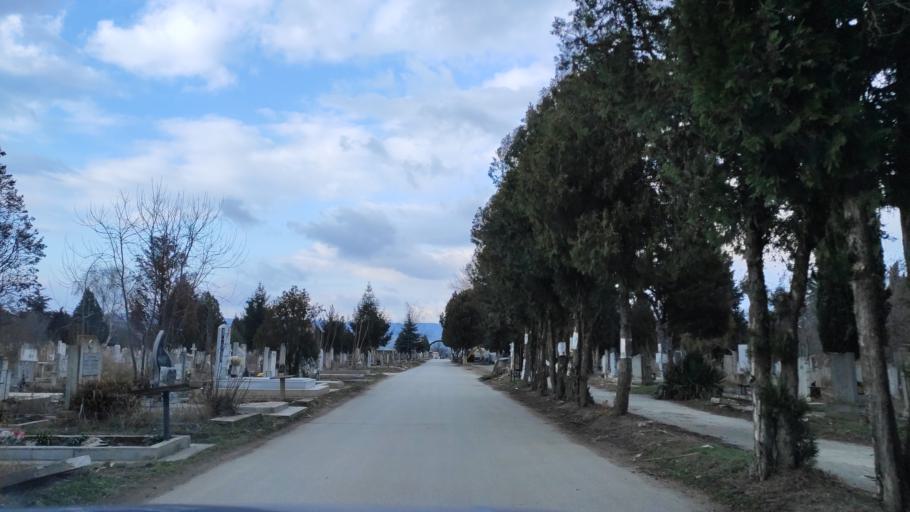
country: BG
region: Varna
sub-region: Obshtina Aksakovo
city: Aksakovo
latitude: 43.2225
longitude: 27.8060
